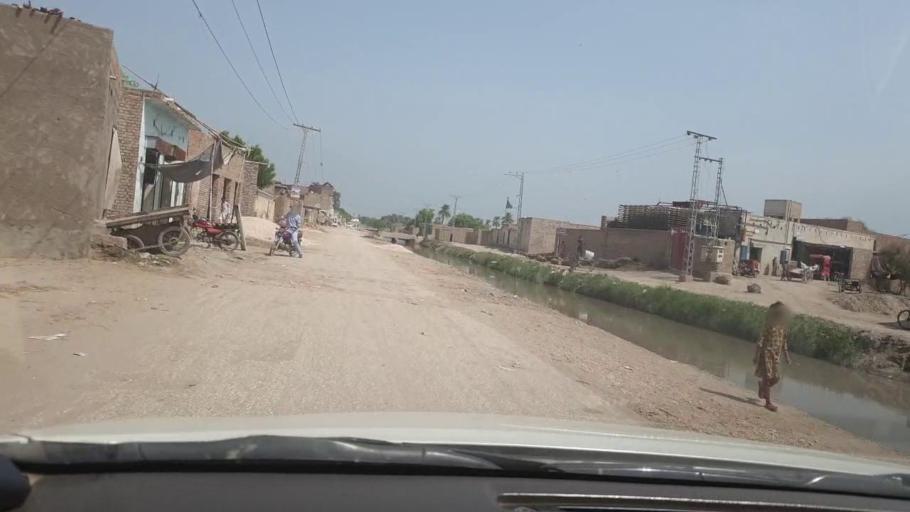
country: PK
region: Sindh
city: Shikarpur
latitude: 27.9449
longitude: 68.6332
